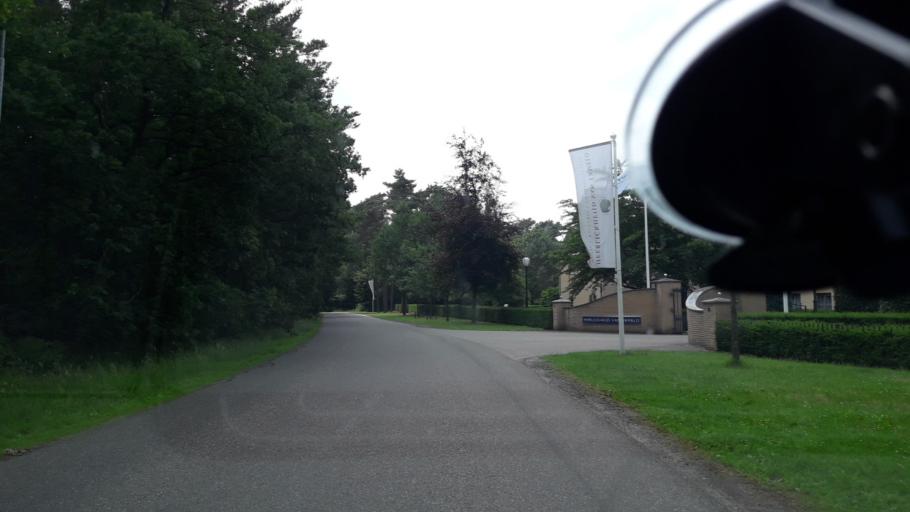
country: NL
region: Gelderland
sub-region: Gemeente Ermelo
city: Ermelo
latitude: 52.3092
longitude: 5.6354
